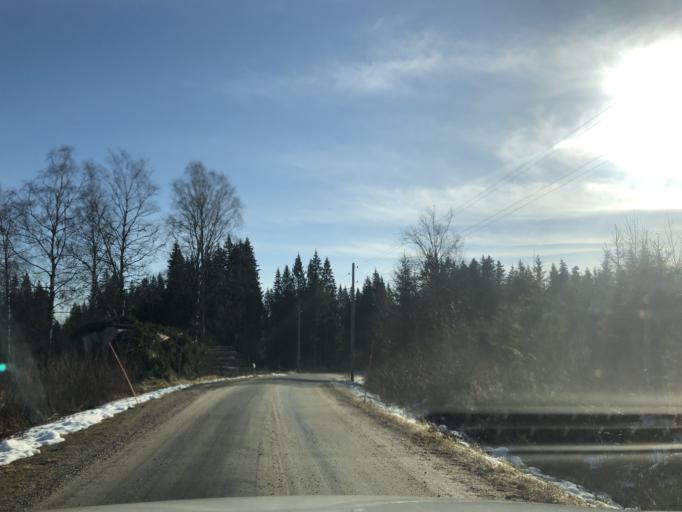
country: SE
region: Vaestra Goetaland
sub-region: Ulricehamns Kommun
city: Ulricehamn
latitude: 57.7956
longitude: 13.4536
